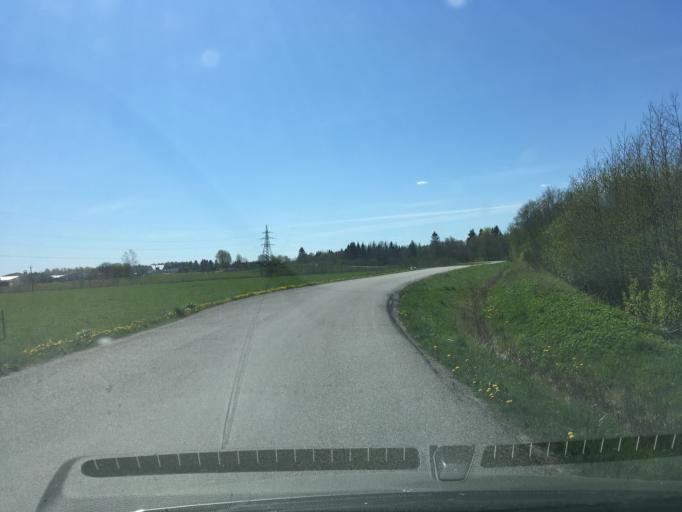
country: EE
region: Harju
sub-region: Raasiku vald
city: Arukula
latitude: 59.3859
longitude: 25.0799
